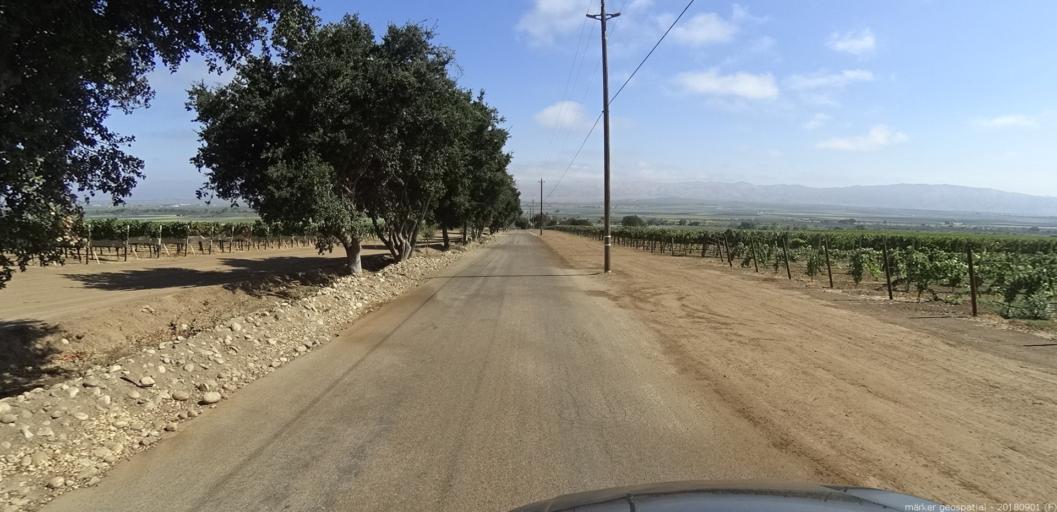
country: US
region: California
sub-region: Monterey County
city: Gonzales
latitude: 36.4643
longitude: -121.4647
